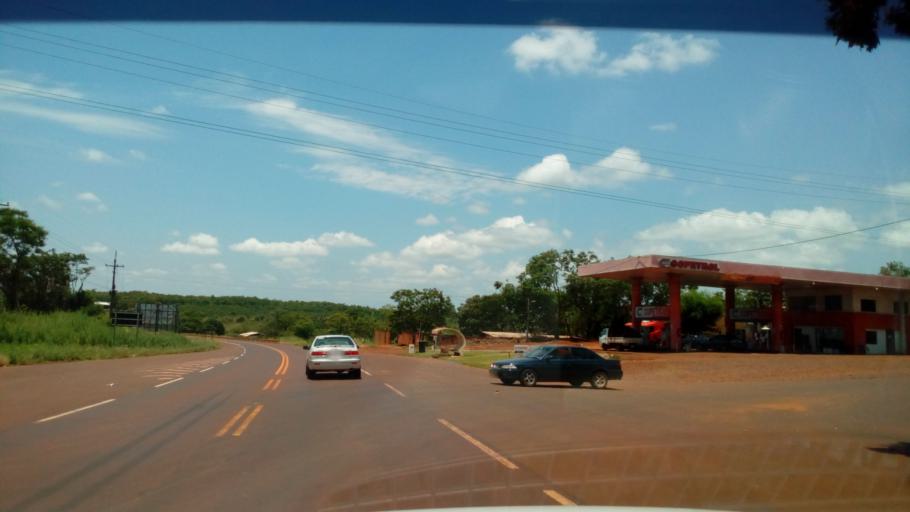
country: PY
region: Alto Parana
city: Naranjal
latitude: -25.9497
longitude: -55.1232
